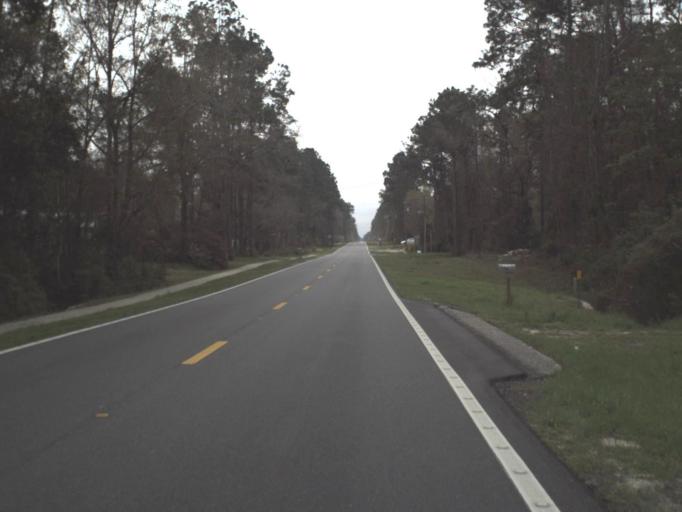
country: US
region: Florida
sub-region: Gulf County
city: Wewahitchka
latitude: 30.0184
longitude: -84.9795
